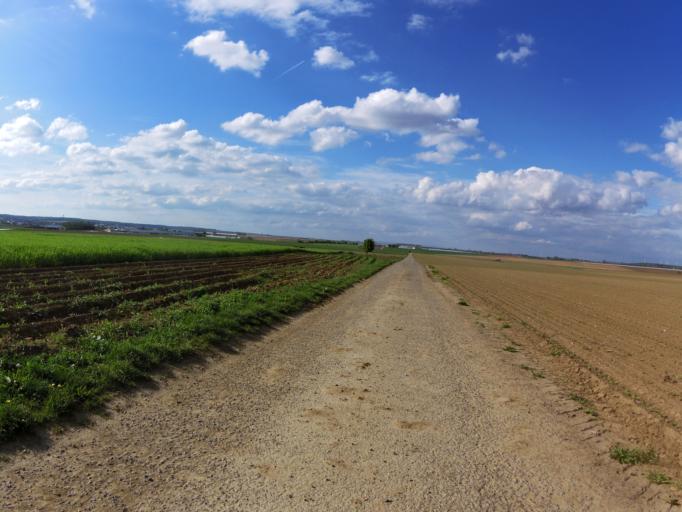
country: DE
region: Bavaria
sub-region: Regierungsbezirk Unterfranken
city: Oberpleichfeld
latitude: 49.8571
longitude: 10.0703
